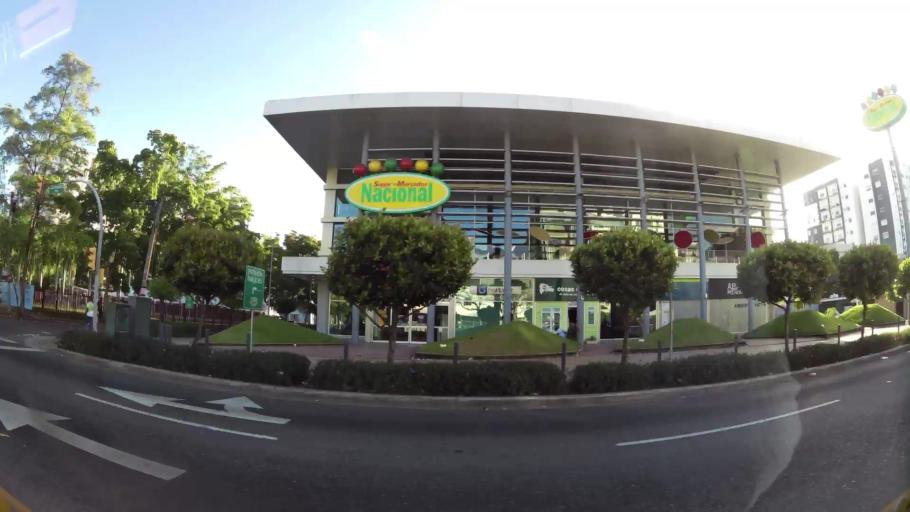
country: DO
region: Nacional
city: La Julia
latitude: 18.4724
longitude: -69.9255
